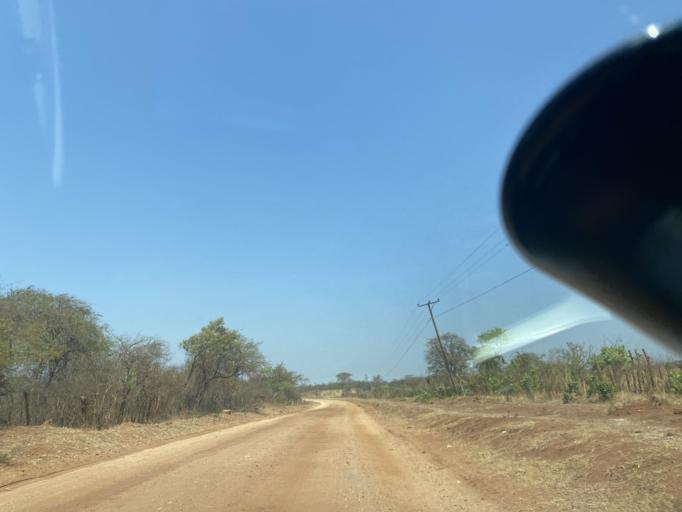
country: ZM
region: Lusaka
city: Lusaka
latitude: -15.5394
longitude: 28.0792
